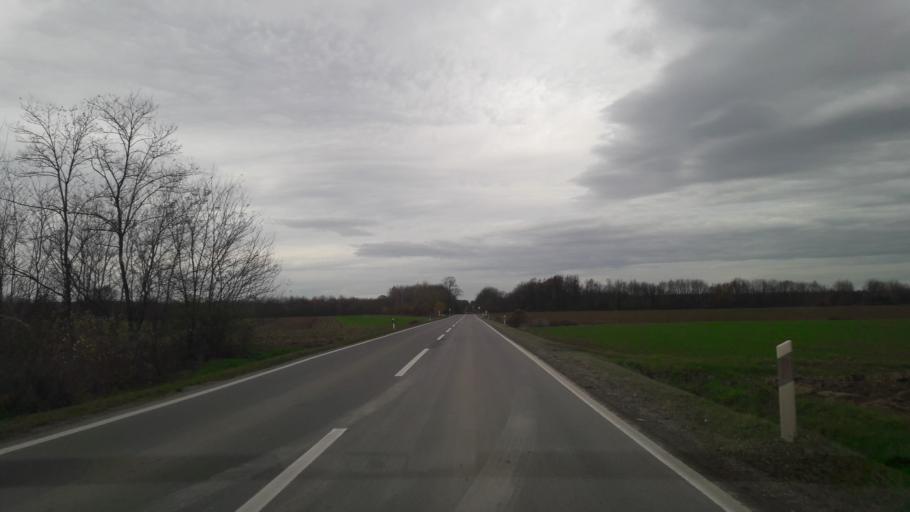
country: HR
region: Osjecko-Baranjska
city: Fericanci
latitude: 45.5339
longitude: 17.9414
